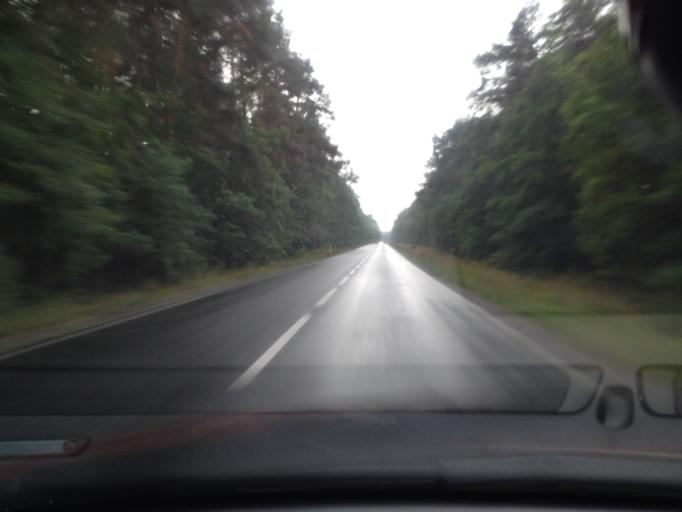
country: PL
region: Lubusz
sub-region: Powiat zaganski
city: Zagan
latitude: 51.5962
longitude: 15.2898
